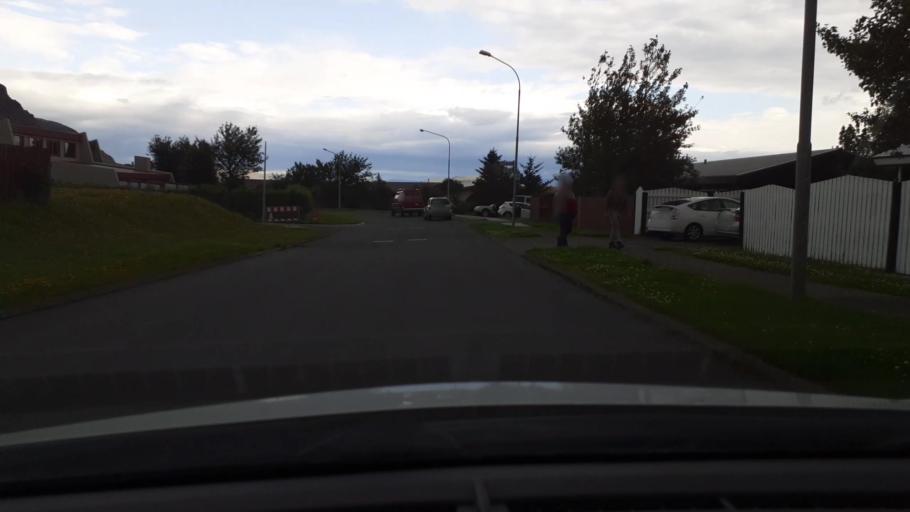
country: IS
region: Capital Region
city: Reykjavik
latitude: 64.2398
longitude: -21.8357
